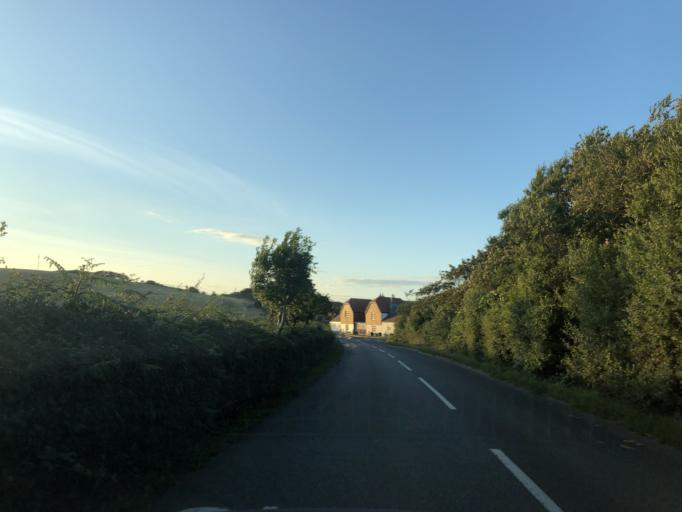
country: GB
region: England
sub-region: Isle of Wight
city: Niton
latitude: 50.6436
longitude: -1.2789
